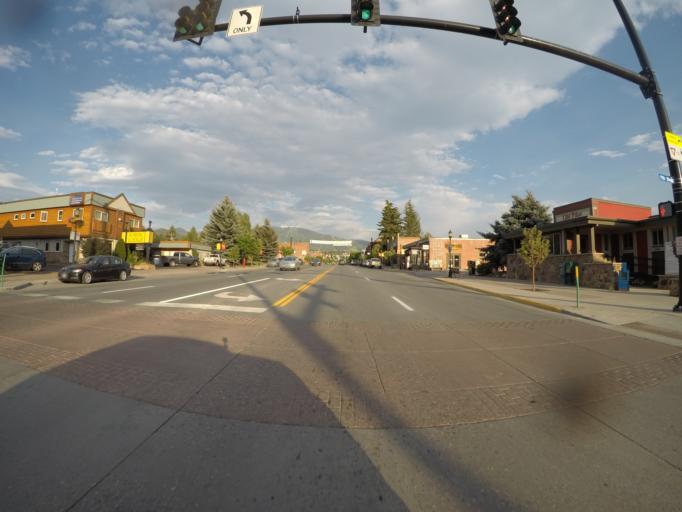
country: US
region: Colorado
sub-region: Routt County
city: Steamboat Springs
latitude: 40.4880
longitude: -106.8379
